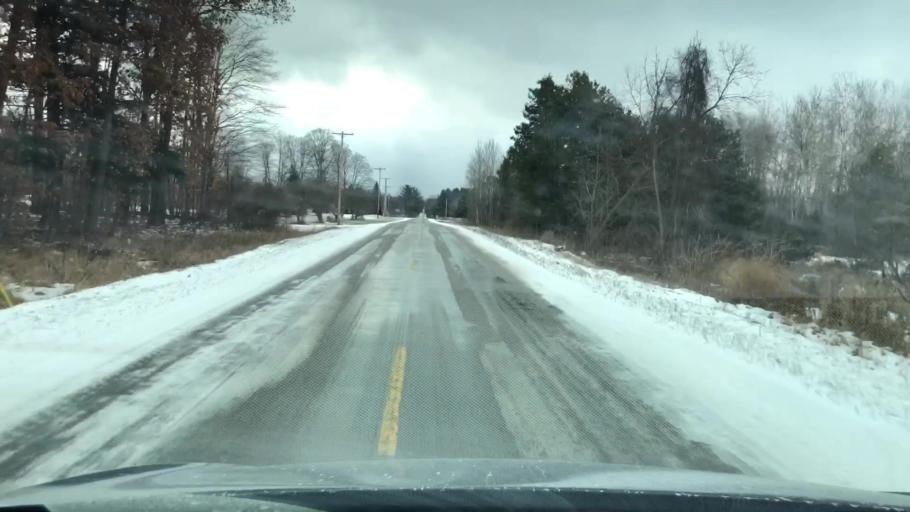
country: US
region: Michigan
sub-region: Antrim County
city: Elk Rapids
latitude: 44.9130
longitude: -85.5154
